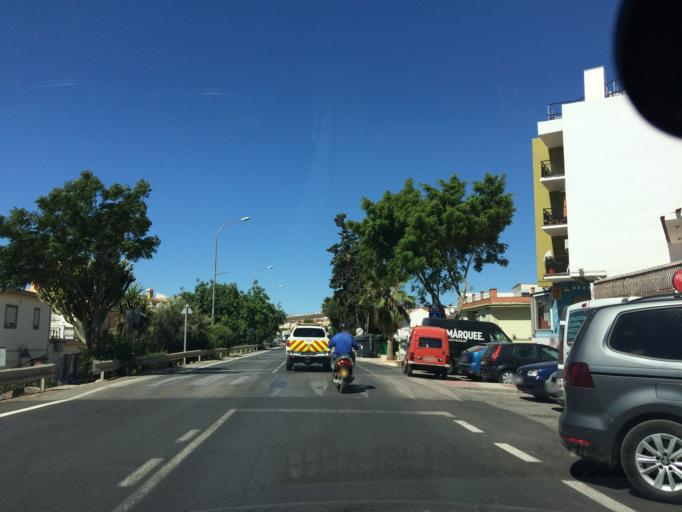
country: ES
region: Andalusia
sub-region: Provincia de Malaga
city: Estacion de Cartama
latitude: 36.7365
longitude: -4.6096
